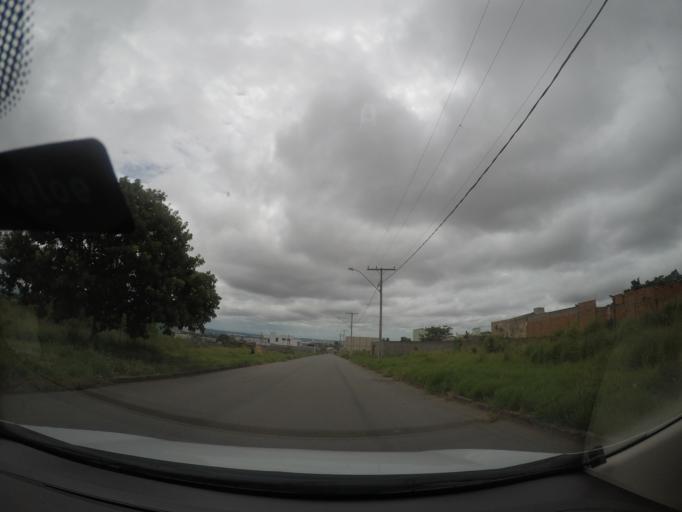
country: BR
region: Goias
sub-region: Goiania
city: Goiania
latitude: -16.7473
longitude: -49.3366
